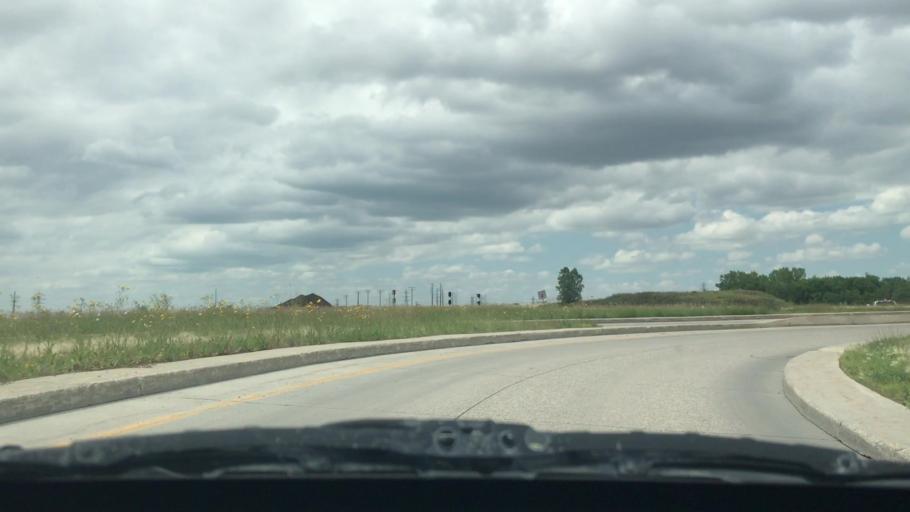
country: CA
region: Manitoba
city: Winnipeg
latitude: 49.8524
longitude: -97.1526
